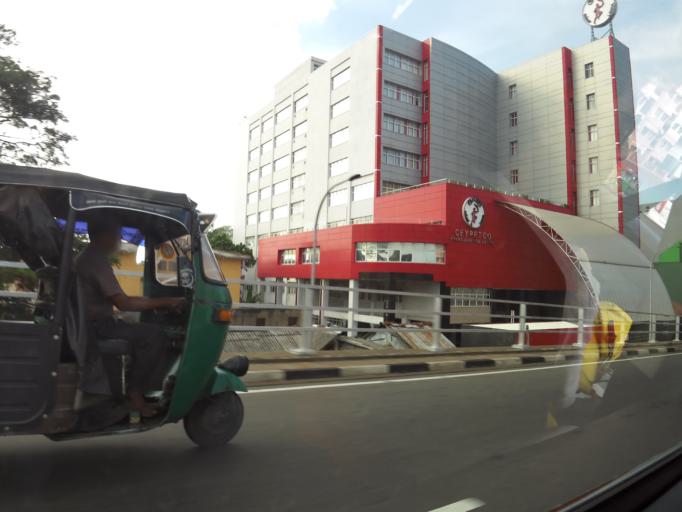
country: LK
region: Western
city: Kolonnawa
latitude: 6.9374
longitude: 79.8782
